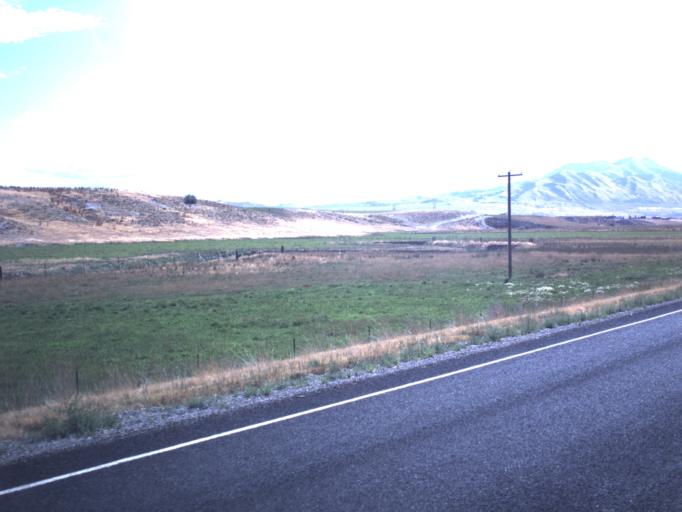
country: US
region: Utah
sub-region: Box Elder County
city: Garland
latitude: 41.8365
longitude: -112.1468
